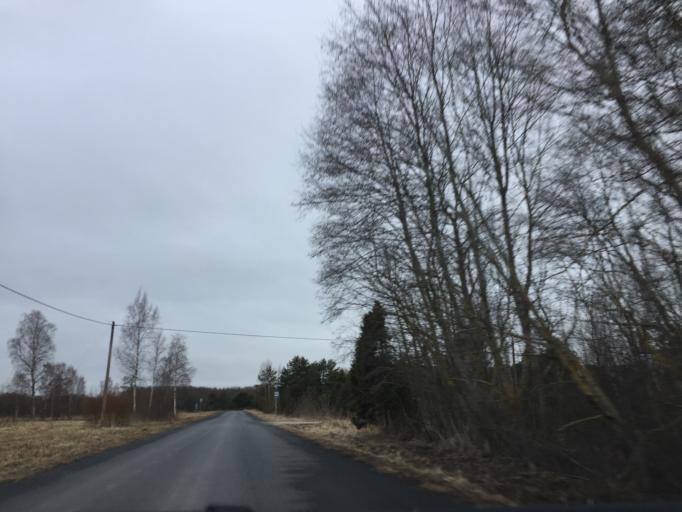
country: EE
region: Laeaene
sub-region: Haapsalu linn
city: Haapsalu
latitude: 58.7949
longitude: 23.4848
